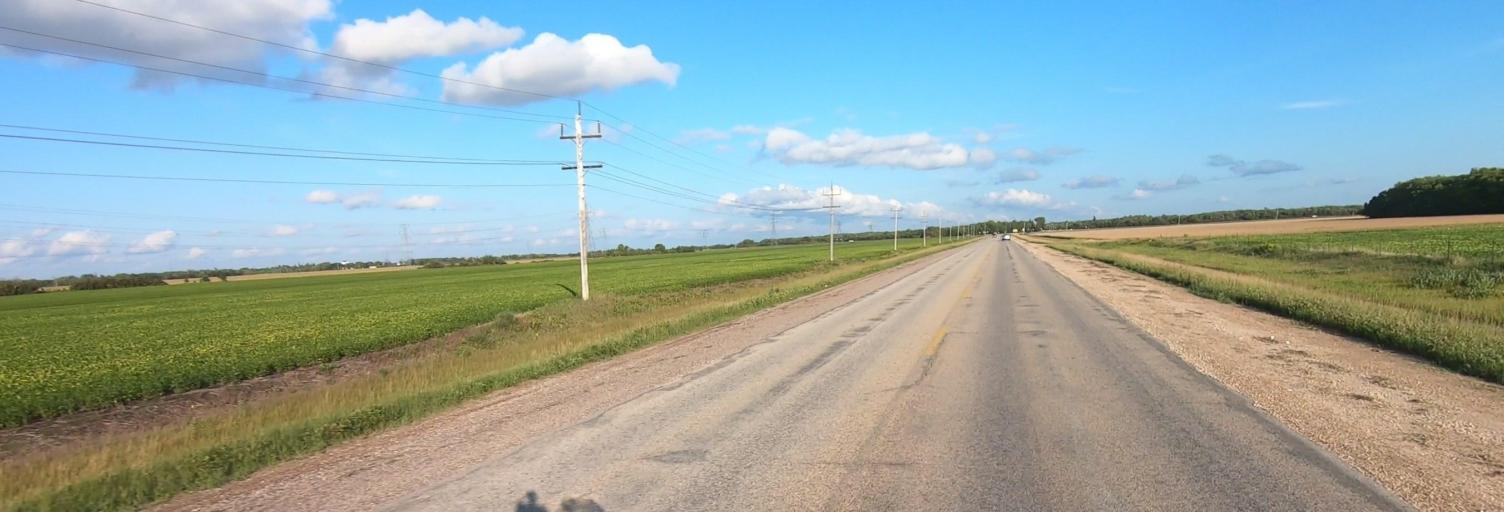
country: CA
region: Manitoba
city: Selkirk
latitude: 50.1185
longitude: -96.8509
